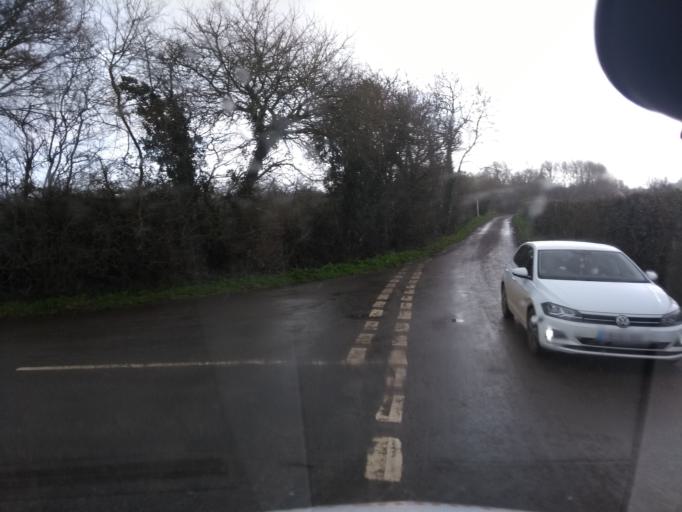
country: GB
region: England
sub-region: Somerset
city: South Petherton
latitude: 50.9735
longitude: -2.8123
